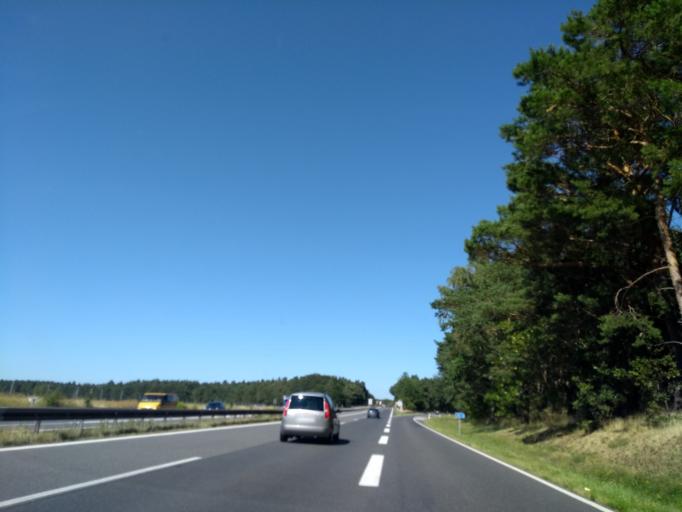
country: DE
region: Brandenburg
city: Lubbenau
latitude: 51.8401
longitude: 13.9206
